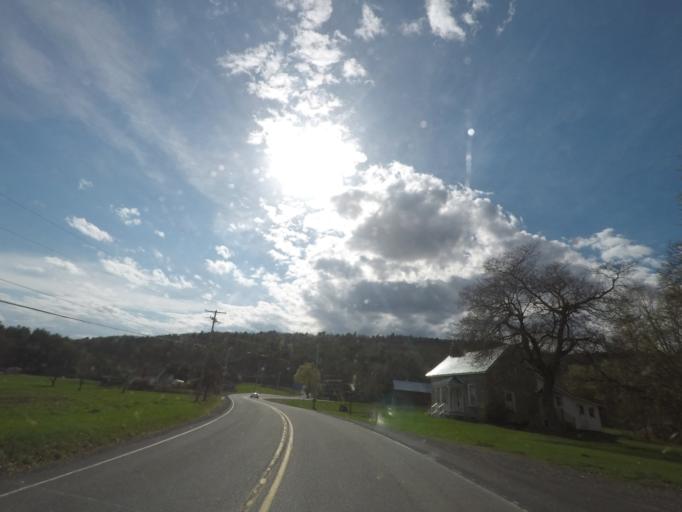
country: US
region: New York
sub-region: Albany County
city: Voorheesville
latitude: 42.5593
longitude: -73.9496
